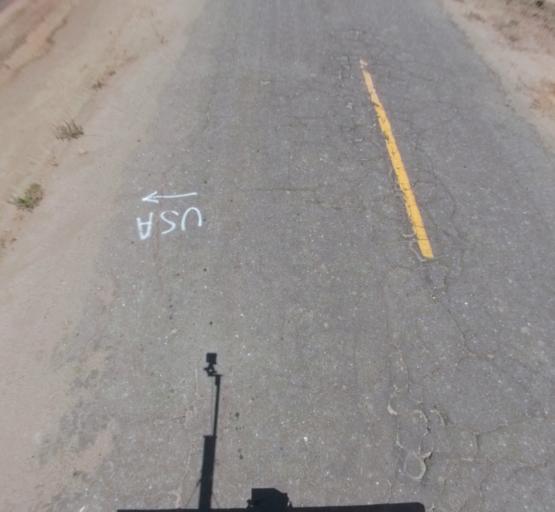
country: US
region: California
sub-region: Madera County
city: Chowchilla
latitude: 37.0617
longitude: -120.3079
